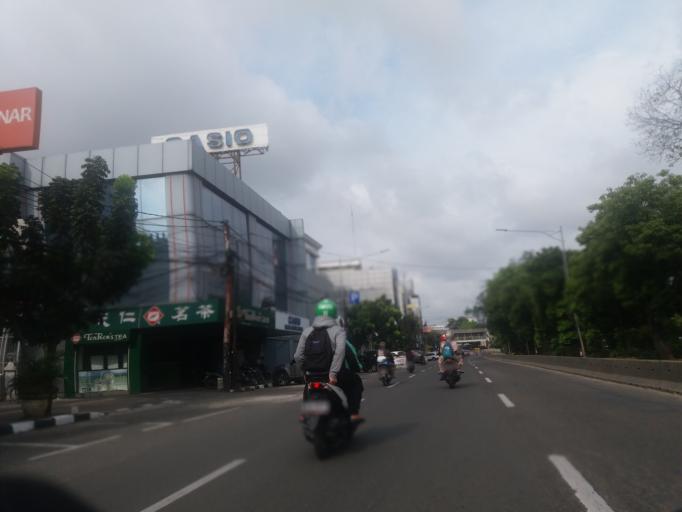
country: ID
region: Jakarta Raya
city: Jakarta
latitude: -6.1675
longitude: 106.8282
